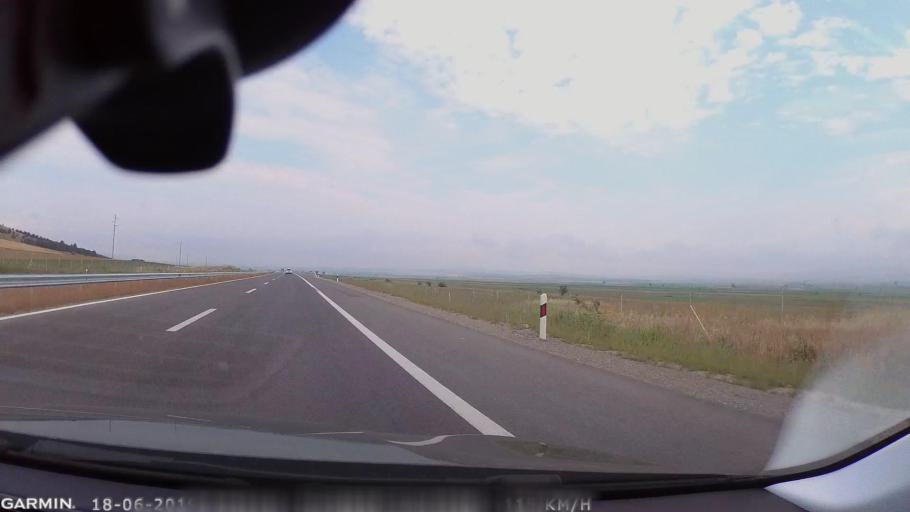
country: MK
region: Stip
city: Shtip
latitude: 41.8032
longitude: 22.0726
